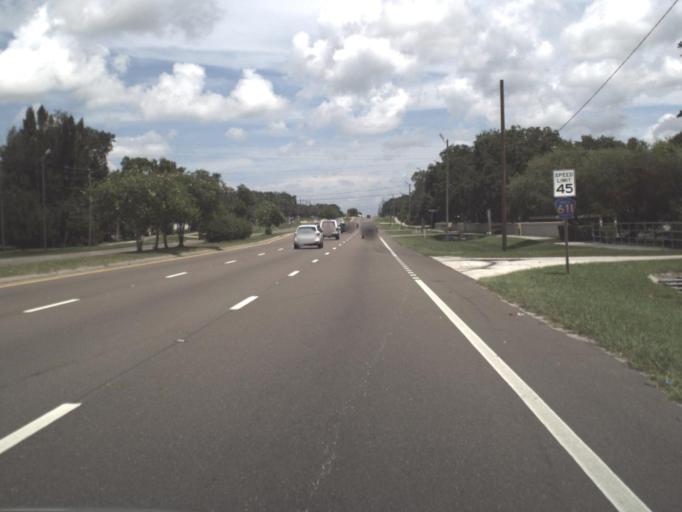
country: US
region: Florida
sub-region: Pinellas County
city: Safety Harbor
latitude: 27.9976
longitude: -82.7087
